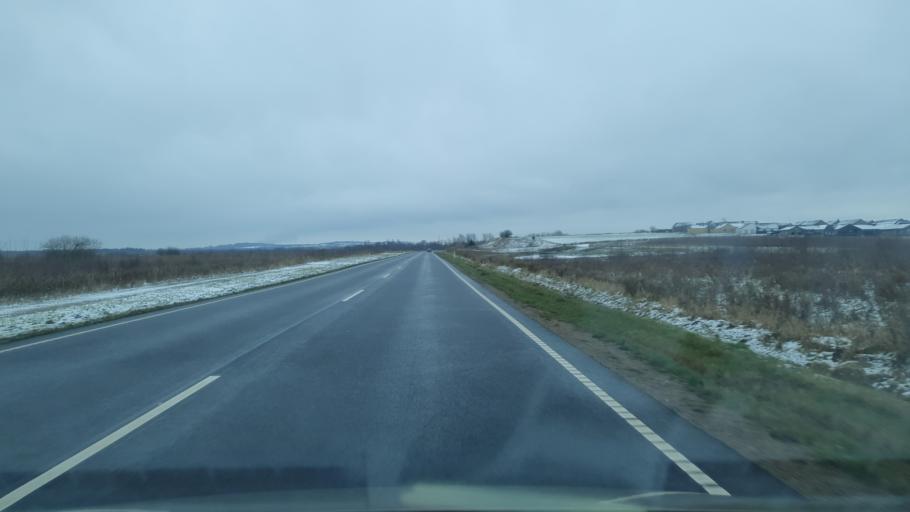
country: DK
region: North Denmark
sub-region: Alborg Kommune
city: Frejlev
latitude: 57.0132
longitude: 9.8058
